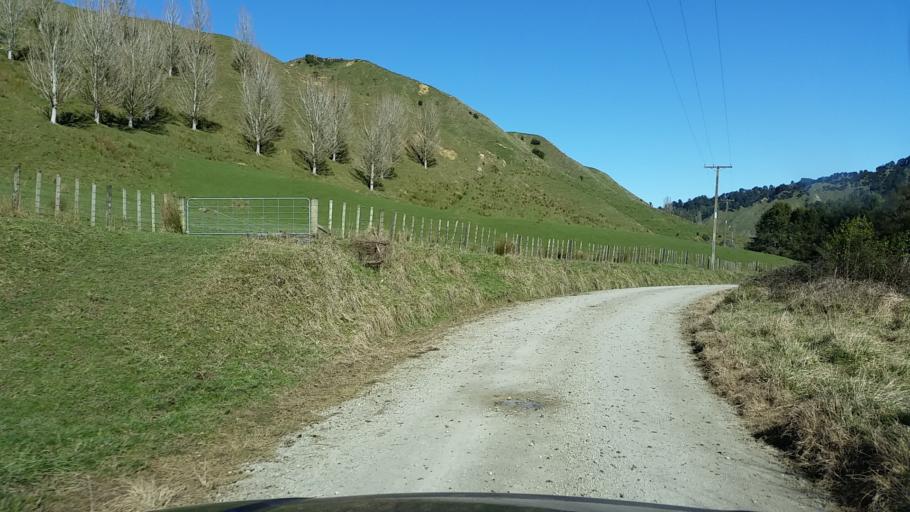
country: NZ
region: Manawatu-Wanganui
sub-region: Wanganui District
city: Wanganui
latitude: -39.5395
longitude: 174.9156
